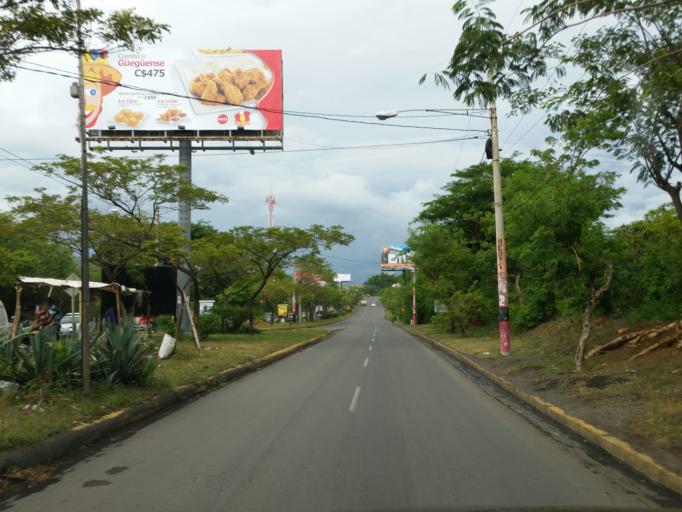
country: NI
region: Managua
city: Ciudad Sandino
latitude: 12.1163
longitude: -86.3149
